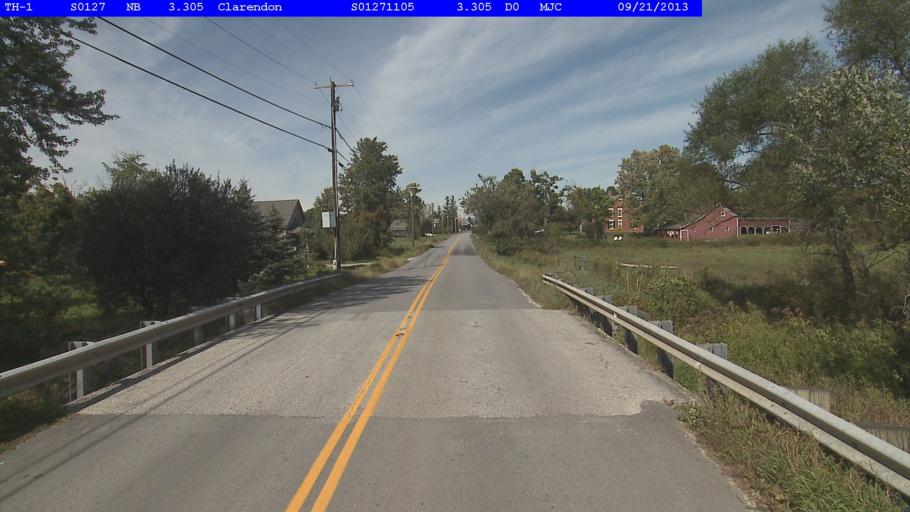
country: US
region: Vermont
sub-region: Rutland County
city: Rutland
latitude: 43.5609
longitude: -72.9722
